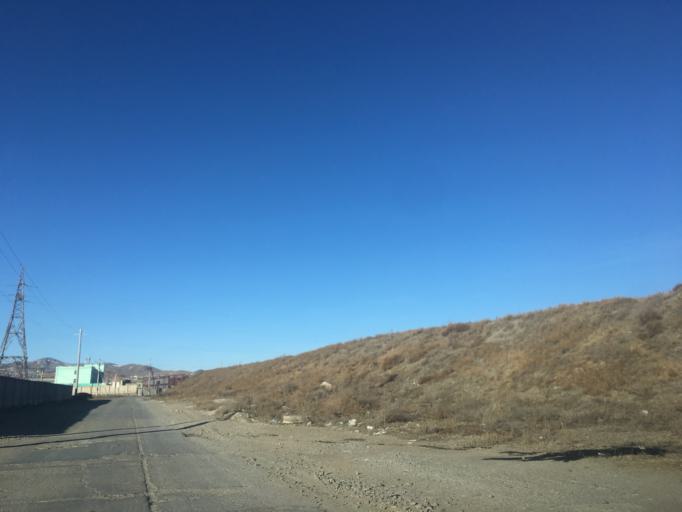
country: MN
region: Ulaanbaatar
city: Ulaanbaatar
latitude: 47.8999
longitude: 106.7970
